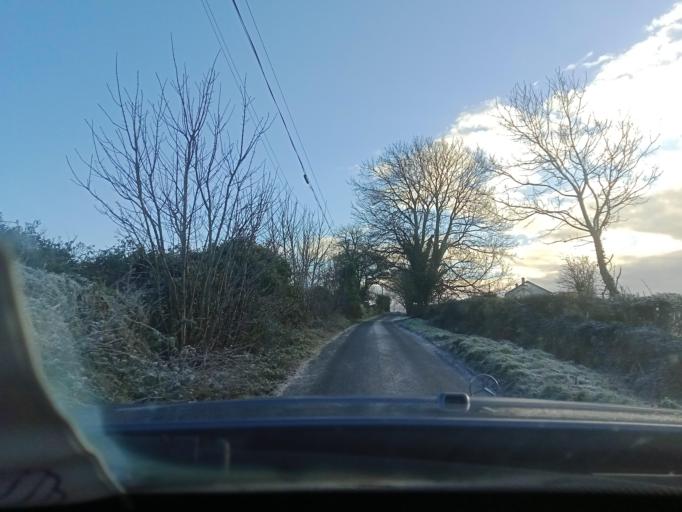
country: IE
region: Leinster
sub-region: Kilkenny
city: Graiguenamanagh
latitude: 52.6002
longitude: -6.9866
